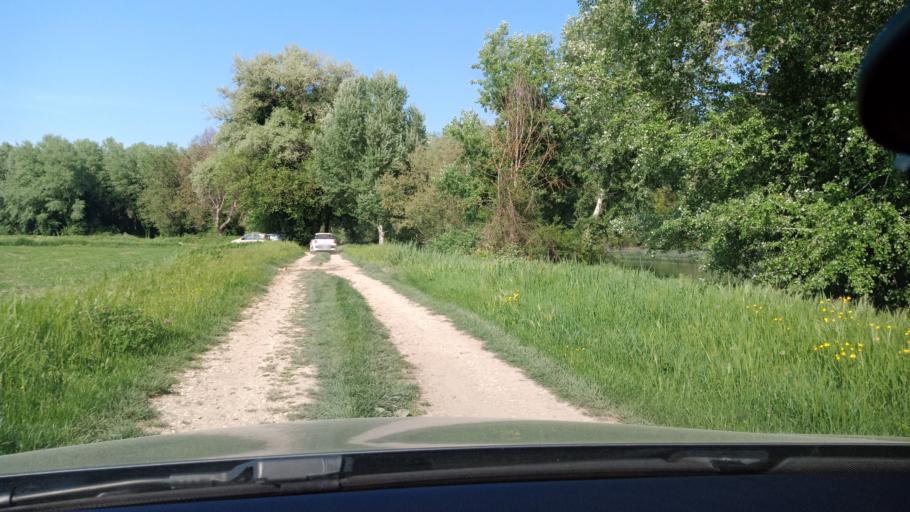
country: IT
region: Latium
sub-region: Provincia di Rieti
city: Forano
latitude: 42.2805
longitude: 12.5839
